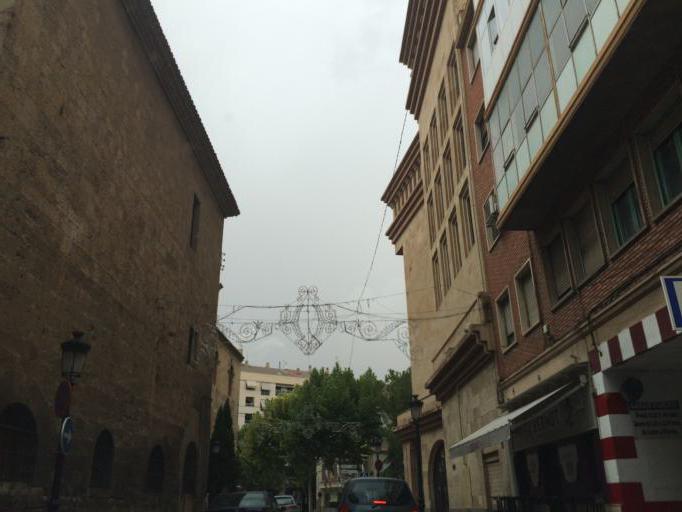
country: ES
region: Castille-La Mancha
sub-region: Provincia de Albacete
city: Albacete
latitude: 38.9958
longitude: -1.8553
